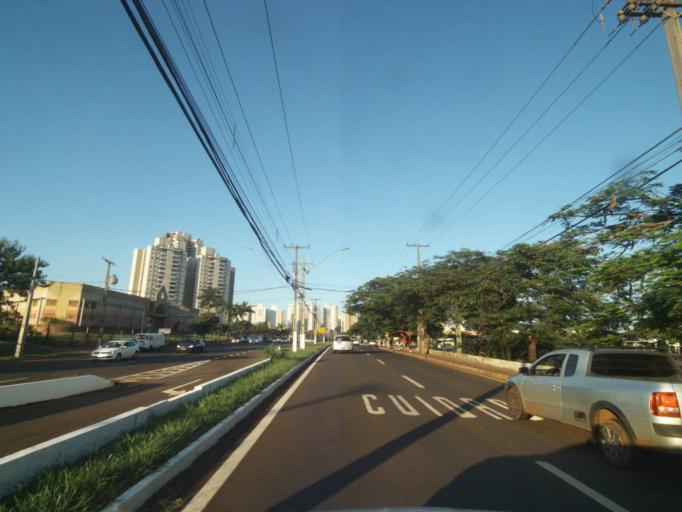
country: BR
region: Parana
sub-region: Londrina
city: Londrina
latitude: -23.3402
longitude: -51.1873
